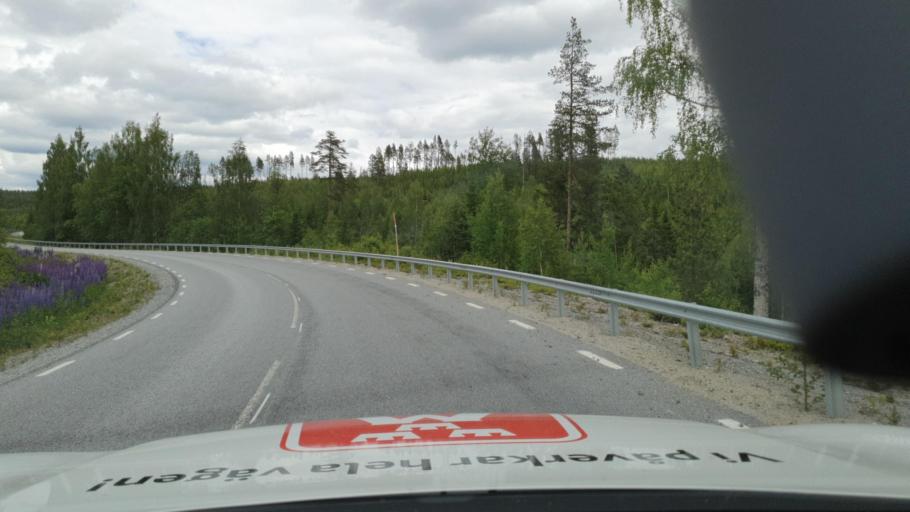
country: SE
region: Vaesterbotten
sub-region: Bjurholms Kommun
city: Bjurholm
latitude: 63.8775
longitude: 19.0139
